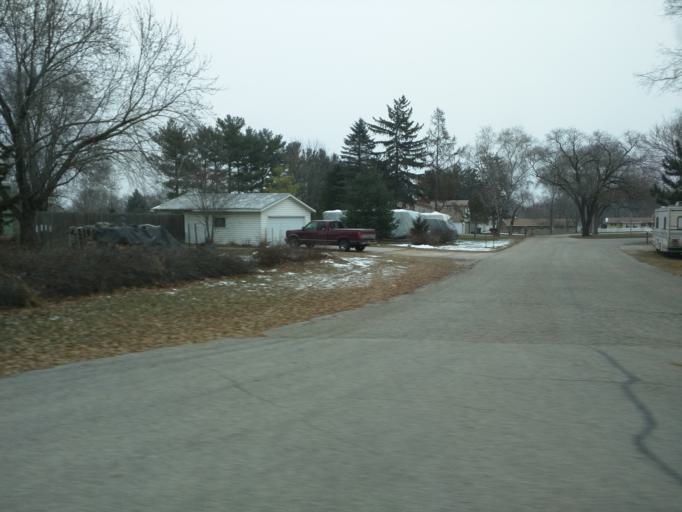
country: US
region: Wisconsin
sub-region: La Crosse County
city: French Island
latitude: 43.8556
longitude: -91.2695
